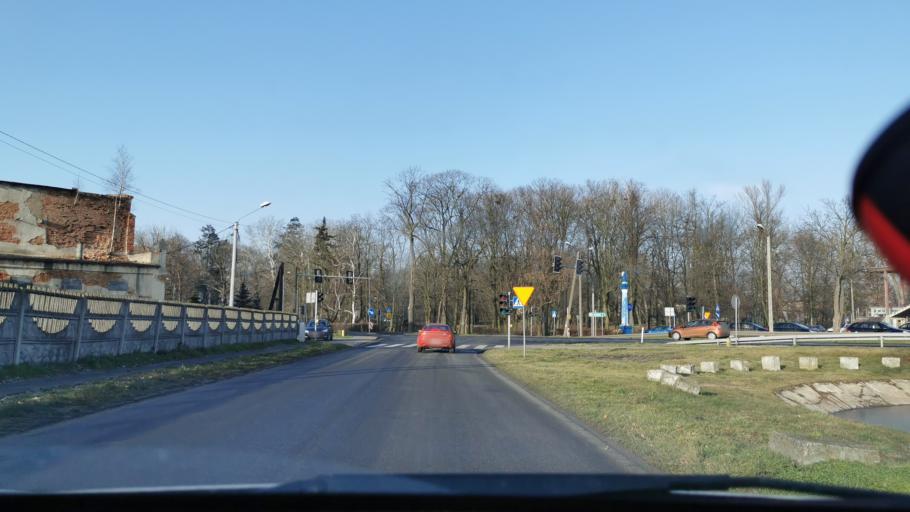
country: PL
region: Lodz Voivodeship
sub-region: Powiat sieradzki
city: Blaszki
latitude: 51.6853
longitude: 18.3287
